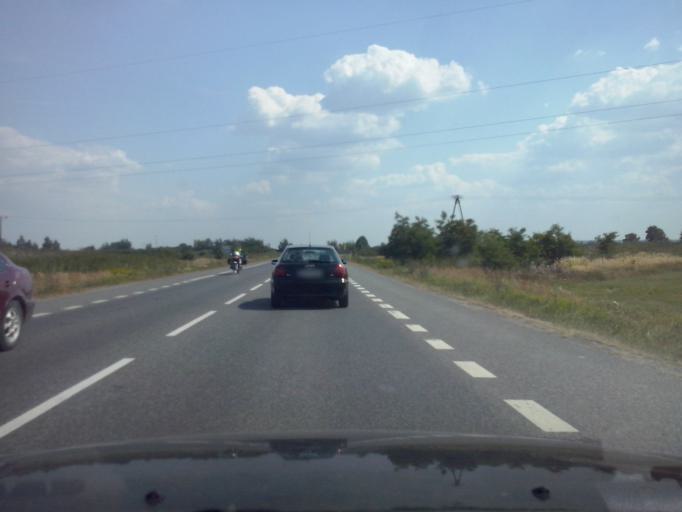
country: PL
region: Swietokrzyskie
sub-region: Powiat sandomierski
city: Loniow
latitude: 50.5419
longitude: 21.5626
